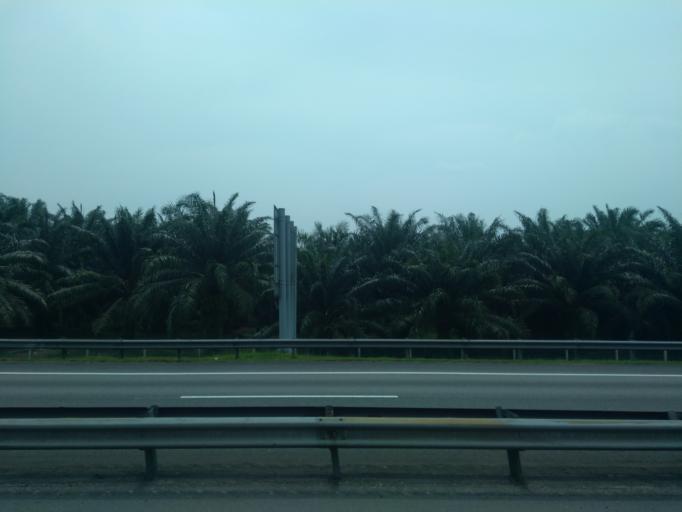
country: MY
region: Perak
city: Simpang Empat
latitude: 4.9116
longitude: 100.6696
